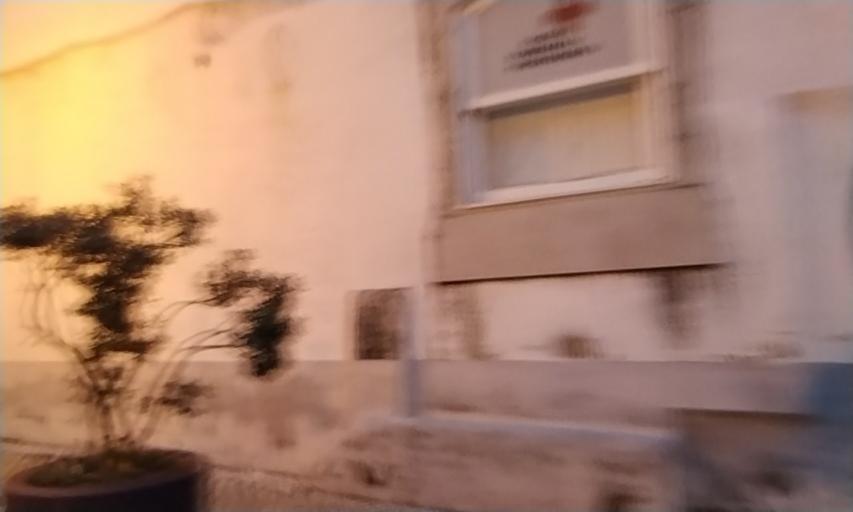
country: PT
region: Setubal
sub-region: Setubal
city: Setubal
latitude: 38.5240
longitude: -8.8897
